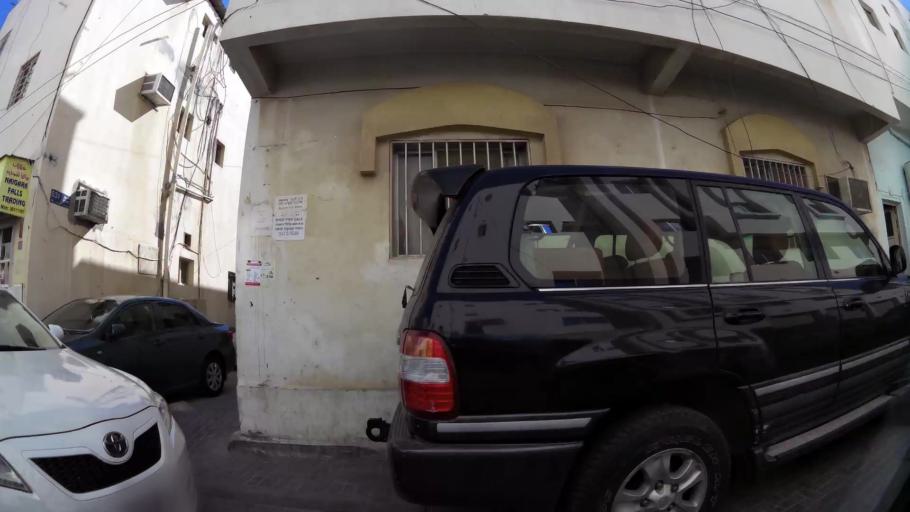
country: BH
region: Muharraq
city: Al Muharraq
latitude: 26.2569
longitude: 50.6113
